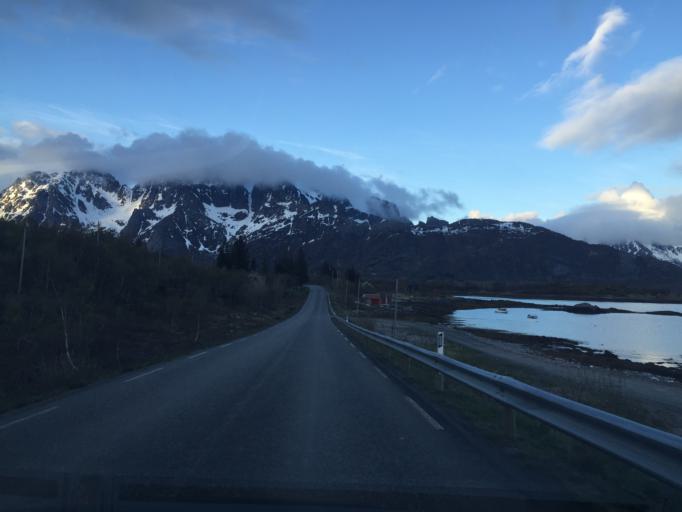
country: NO
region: Nordland
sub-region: Vagan
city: Svolvaer
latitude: 68.2838
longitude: 14.6682
